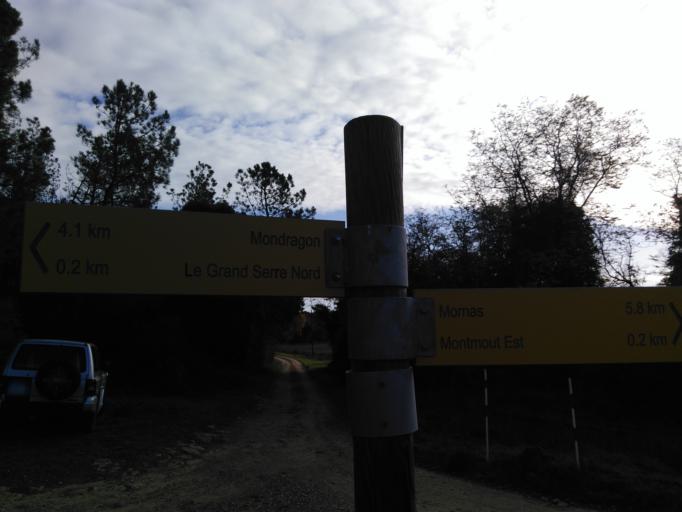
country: FR
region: Provence-Alpes-Cote d'Azur
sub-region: Departement du Vaucluse
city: Mornas
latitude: 44.2277
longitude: 4.7511
